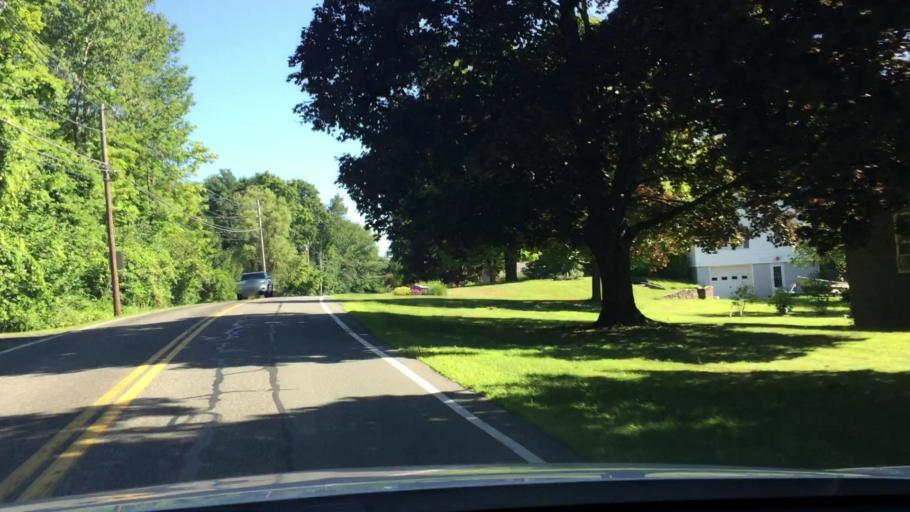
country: US
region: Massachusetts
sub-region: Berkshire County
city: West Stockbridge
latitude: 42.3392
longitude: -73.3671
